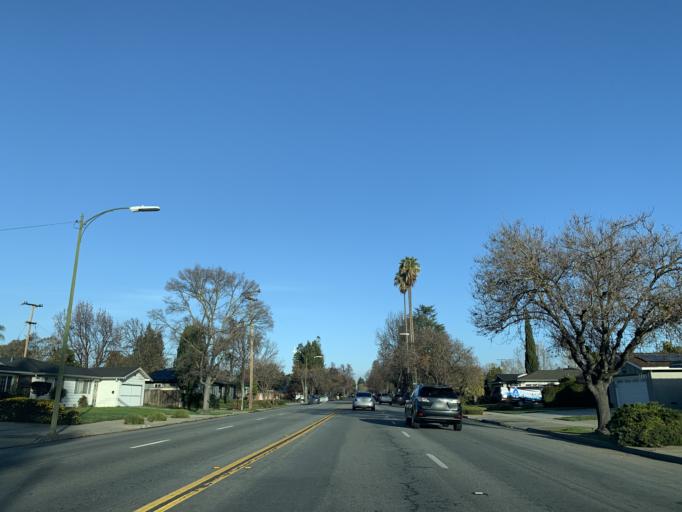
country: US
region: California
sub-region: Santa Clara County
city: Cambrian Park
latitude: 37.2758
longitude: -121.9092
